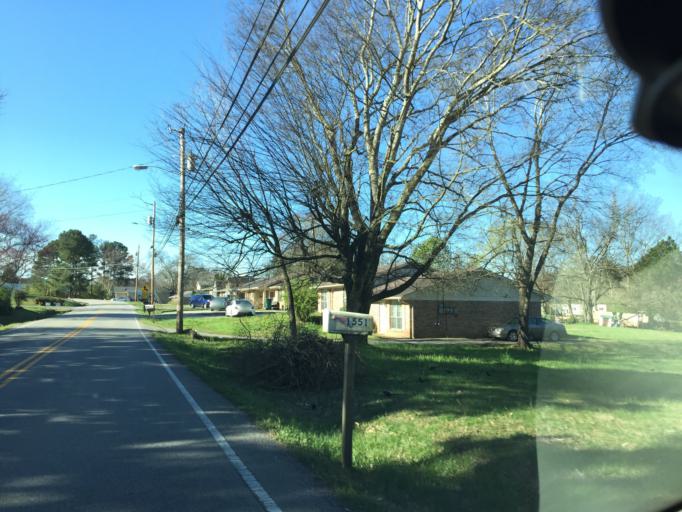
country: US
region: Tennessee
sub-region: Hamilton County
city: East Brainerd
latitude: 35.0229
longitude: -85.1722
